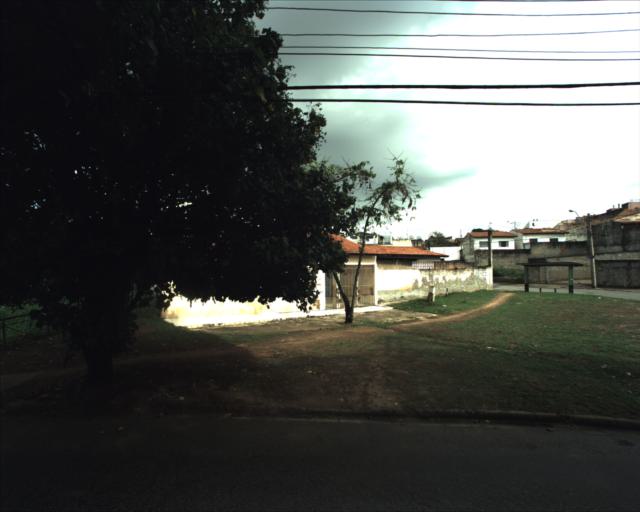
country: BR
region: Sao Paulo
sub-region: Sorocaba
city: Sorocaba
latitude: -23.5030
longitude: -47.5012
